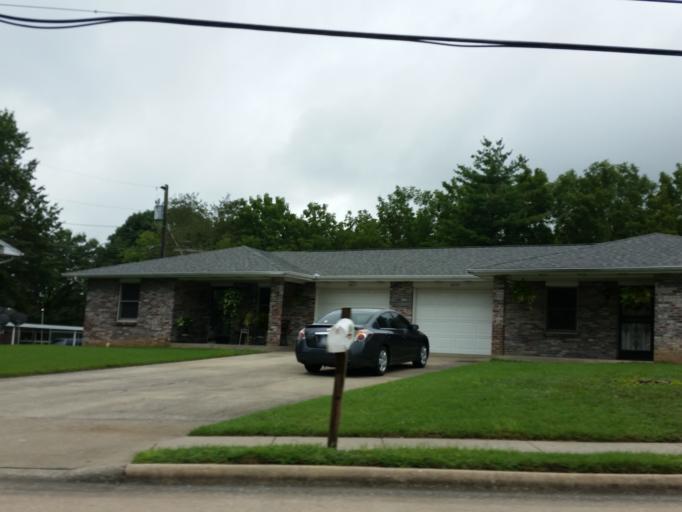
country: US
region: Missouri
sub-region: Cape Girardeau County
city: Cape Girardeau
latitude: 37.3394
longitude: -89.5540
